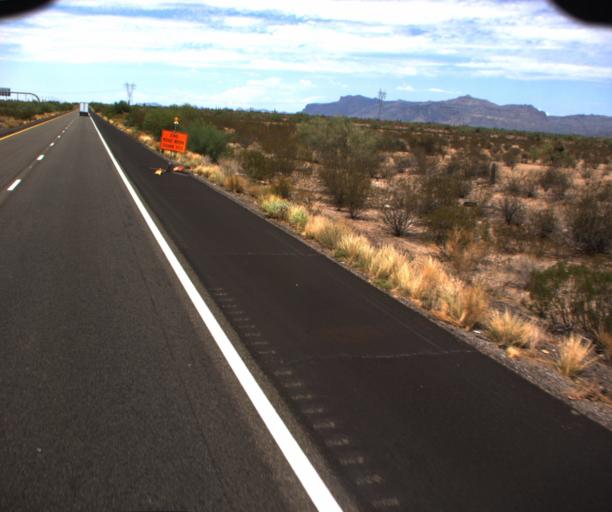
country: US
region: Arizona
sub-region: Pinal County
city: Gold Camp
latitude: 33.2715
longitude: -111.3567
